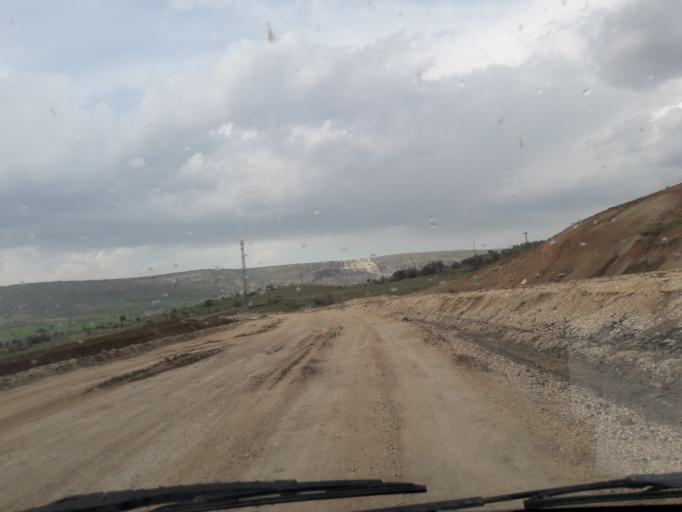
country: TR
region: Giresun
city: Alucra
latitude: 40.3178
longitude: 38.7730
